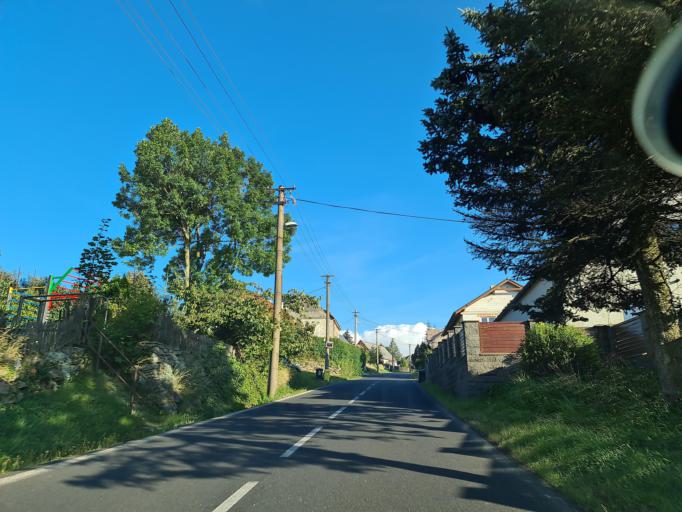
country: DE
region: Saxony
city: Deutschneudorf
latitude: 50.5967
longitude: 13.4793
